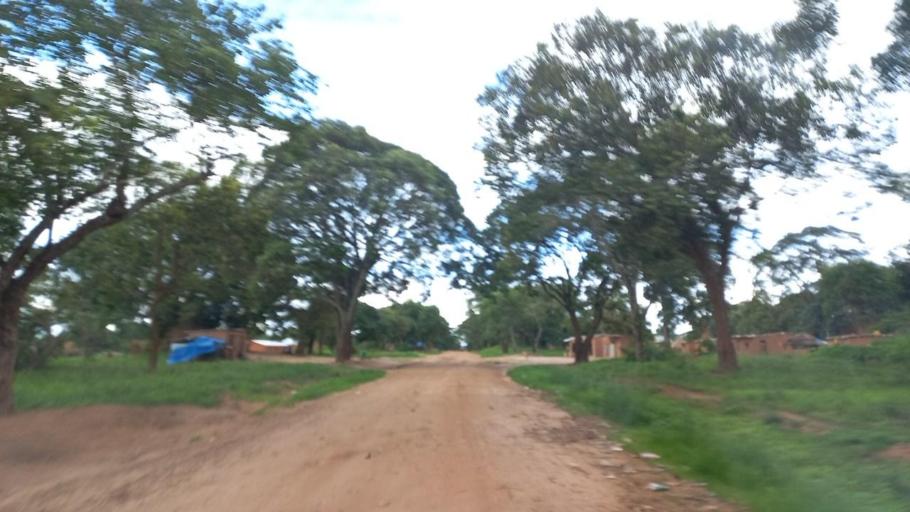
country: ZM
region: North-Western
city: Mwinilunga
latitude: -11.8443
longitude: 24.3641
